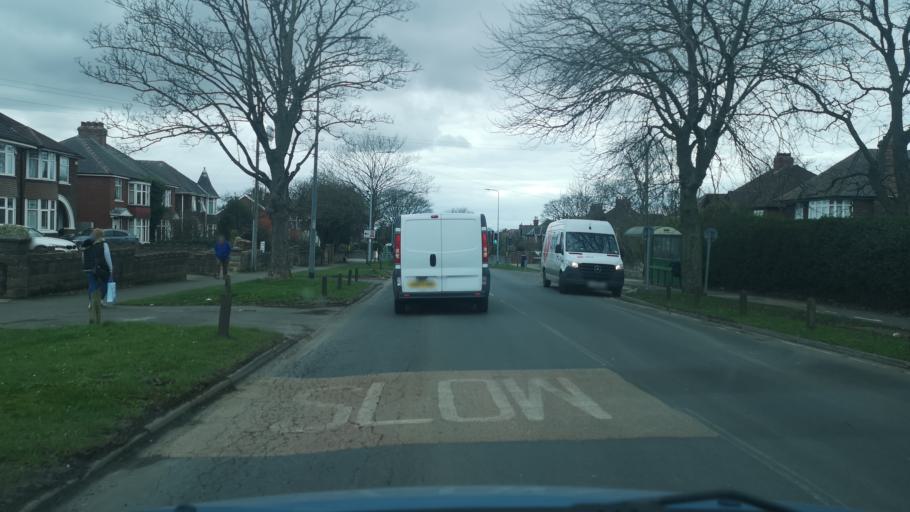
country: GB
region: England
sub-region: North Lincolnshire
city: Scunthorpe
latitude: 53.5903
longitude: -0.6671
